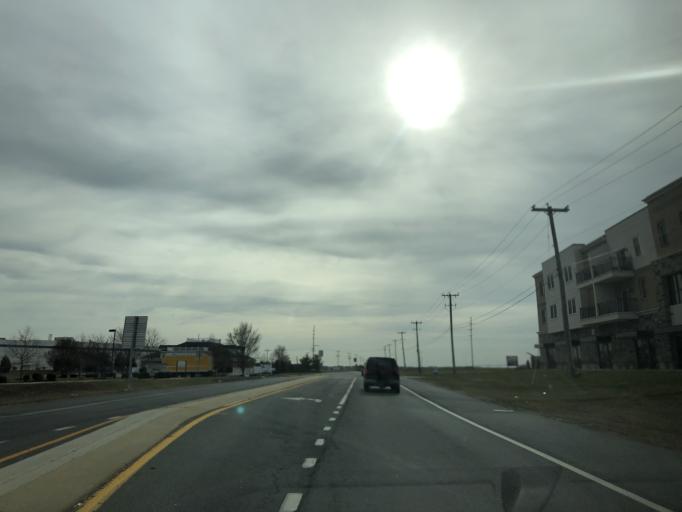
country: US
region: Delaware
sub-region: New Castle County
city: Middletown
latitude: 39.4394
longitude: -75.7462
